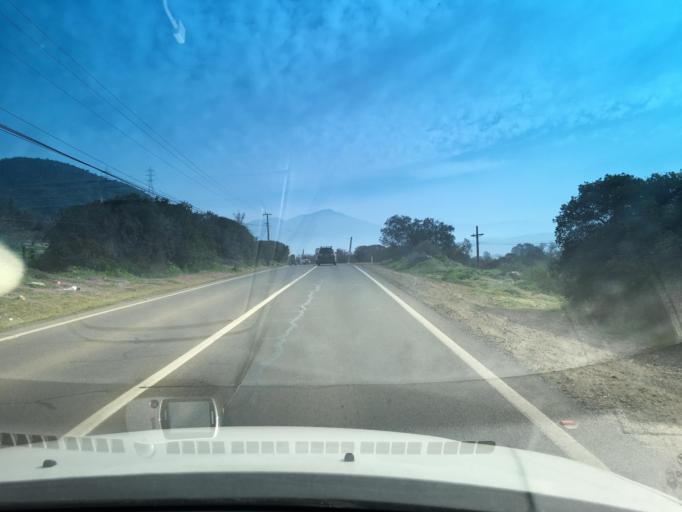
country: CL
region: Santiago Metropolitan
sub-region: Provincia de Chacabuco
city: Lampa
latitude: -33.1464
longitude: -70.9130
